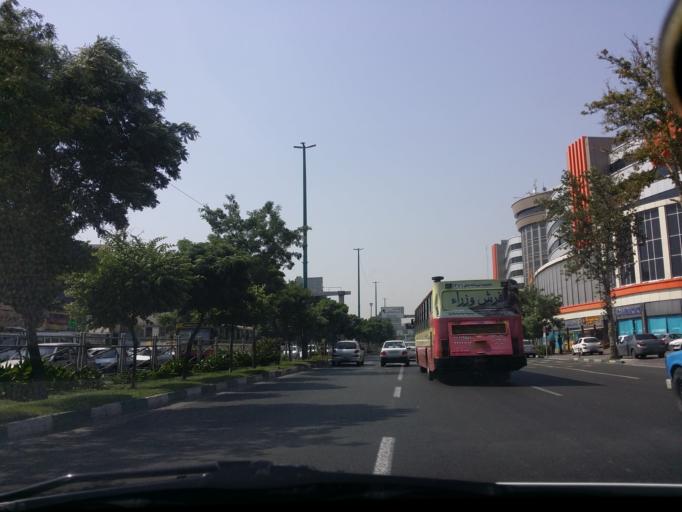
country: IR
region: Alborz
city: Karaj
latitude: 35.7949
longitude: 51.0022
